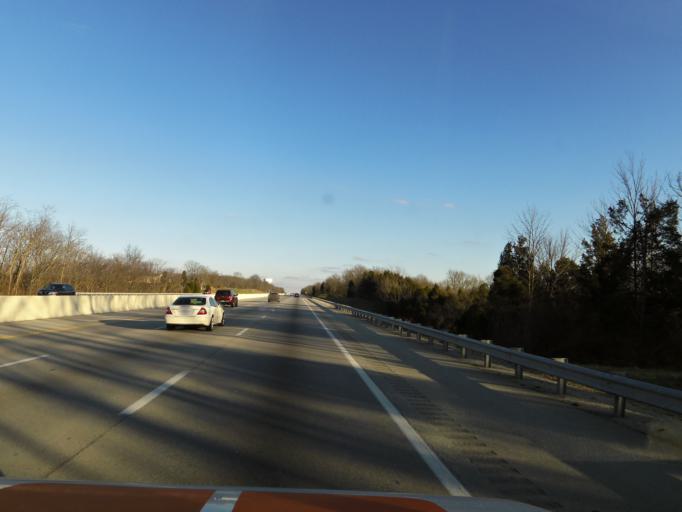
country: US
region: Kentucky
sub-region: Shelby County
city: Simpsonville
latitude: 38.2194
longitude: -85.4365
